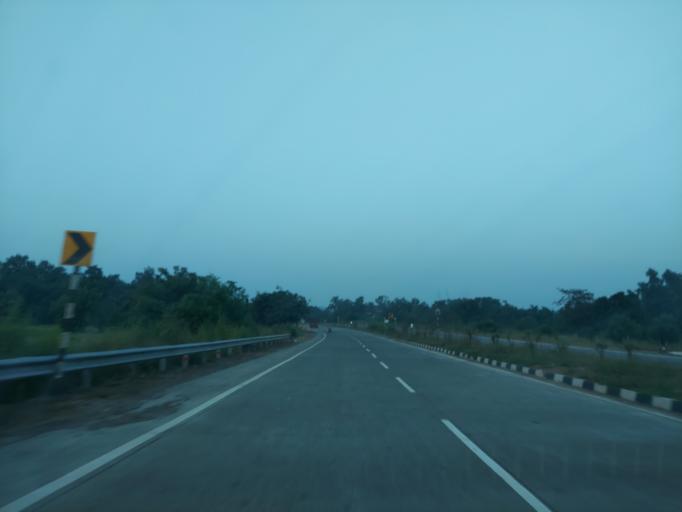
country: IN
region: Maharashtra
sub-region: Sindhudurg
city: Kudal
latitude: 16.0994
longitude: 73.7070
